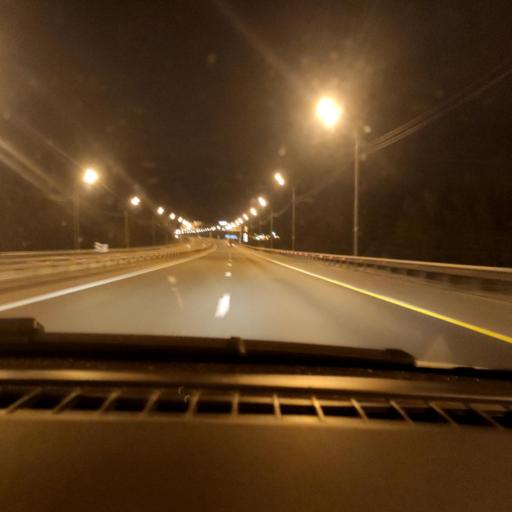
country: RU
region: Lipetsk
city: Khlevnoye
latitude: 52.1452
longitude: 39.2003
